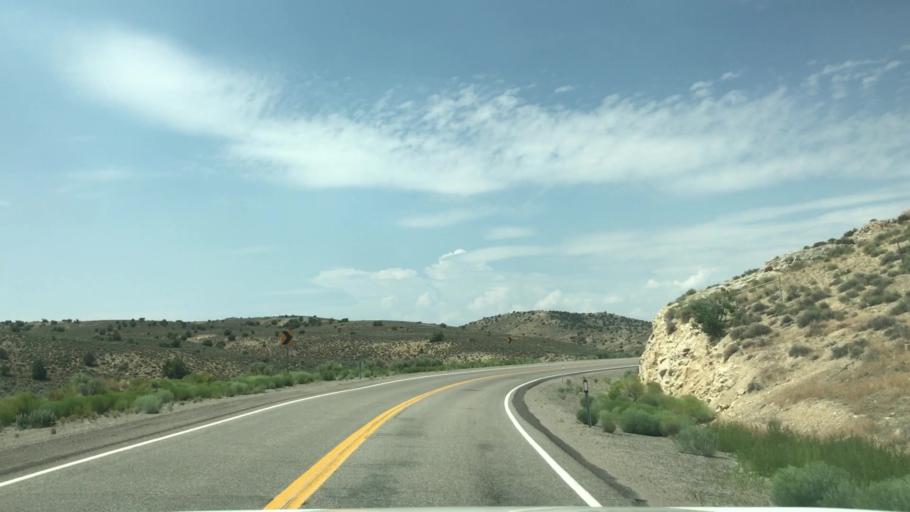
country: US
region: Nevada
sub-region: White Pine County
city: Ely
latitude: 39.3516
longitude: -115.3634
